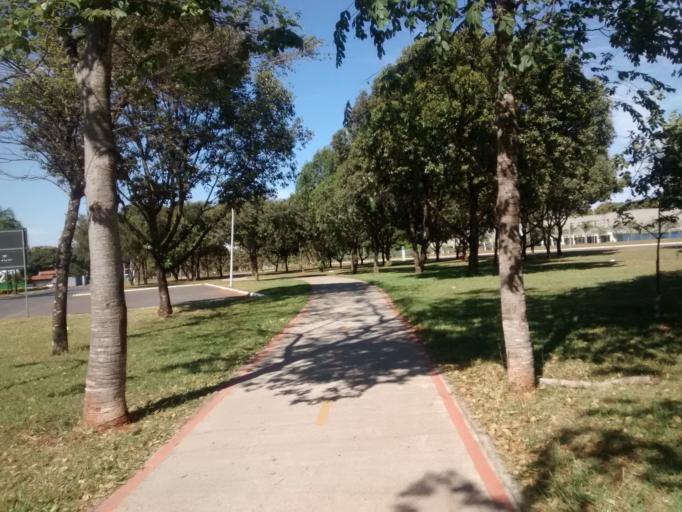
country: BR
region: Federal District
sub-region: Brasilia
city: Brasilia
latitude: -15.7768
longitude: -47.8911
